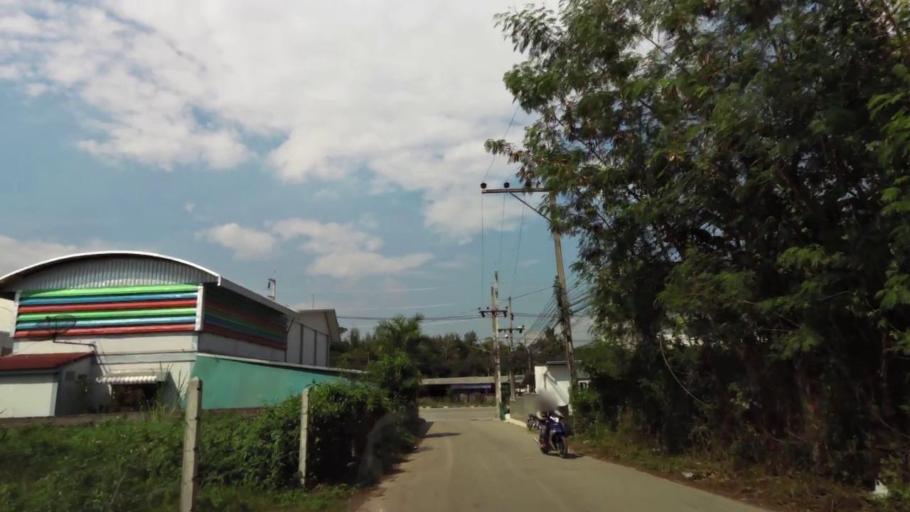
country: TH
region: Chiang Rai
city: Chiang Rai
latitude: 19.8891
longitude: 99.8027
